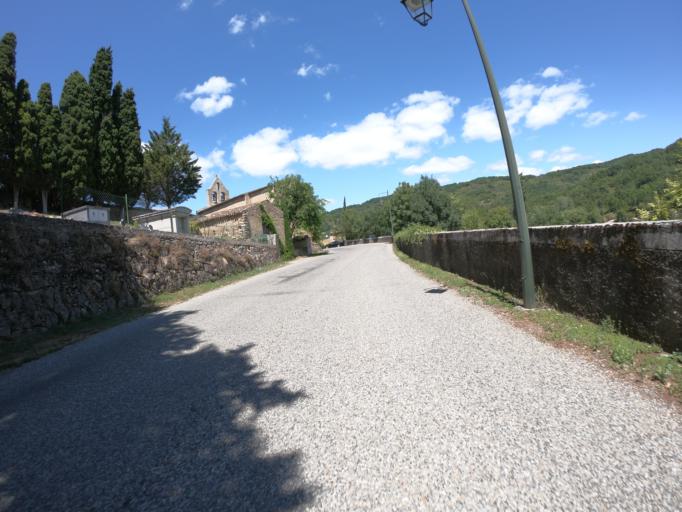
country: FR
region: Midi-Pyrenees
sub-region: Departement de l'Ariege
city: Verniolle
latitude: 43.0501
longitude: 1.7595
